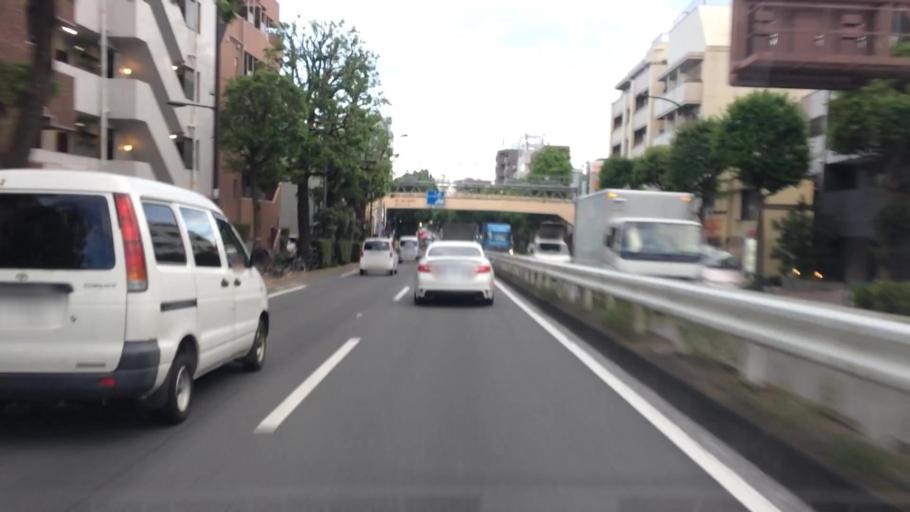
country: JP
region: Tokyo
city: Tokyo
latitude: 35.7150
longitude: 139.6537
